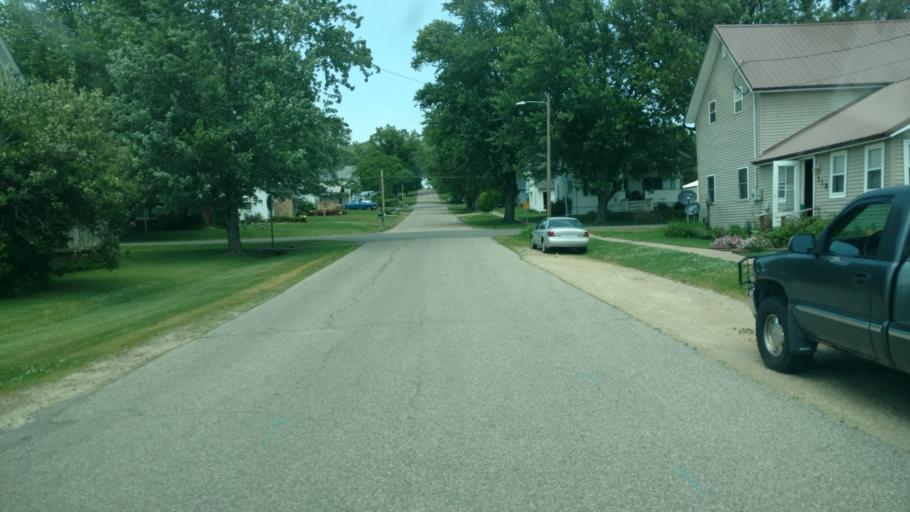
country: US
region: Wisconsin
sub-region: Monroe County
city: Cashton
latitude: 43.5748
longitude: -90.6350
